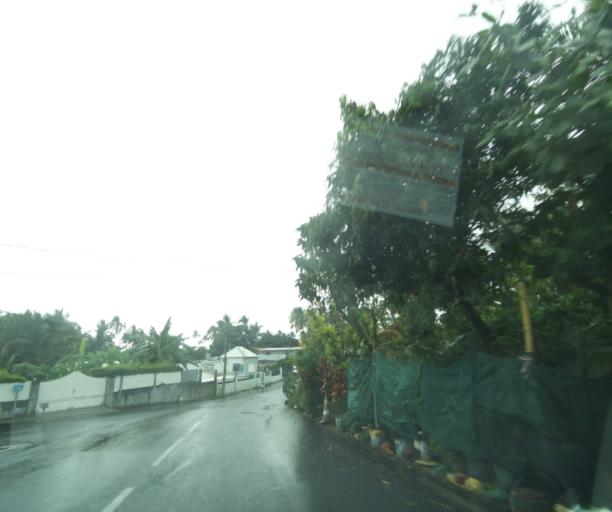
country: RE
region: Reunion
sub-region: Reunion
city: Saint-Paul
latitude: -21.0126
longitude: 55.2758
